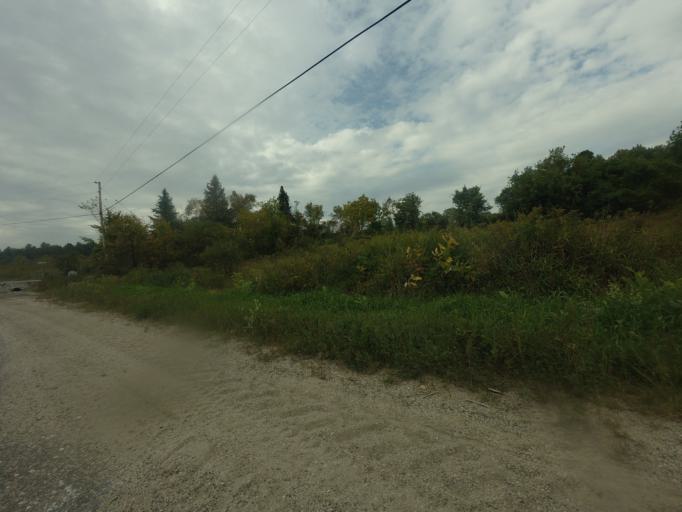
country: CA
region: Quebec
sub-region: Outaouais
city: Wakefield
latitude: 45.9909
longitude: -75.9524
